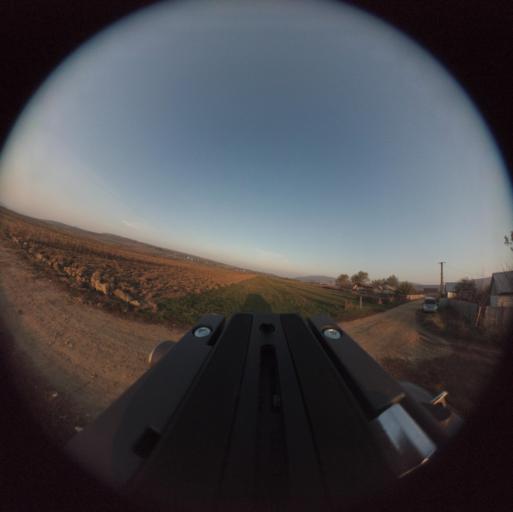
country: RO
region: Vaslui
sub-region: Comuna Bacesti
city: Bacesti
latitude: 46.8330
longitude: 27.2449
